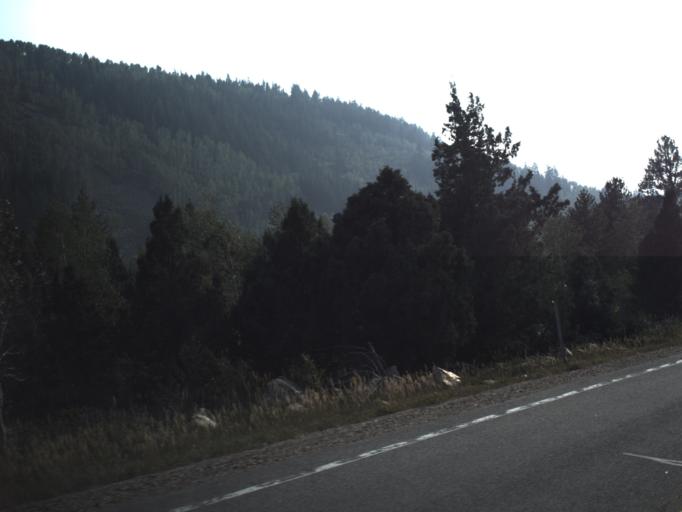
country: US
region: Utah
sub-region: Summit County
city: Francis
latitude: 40.5944
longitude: -111.0862
